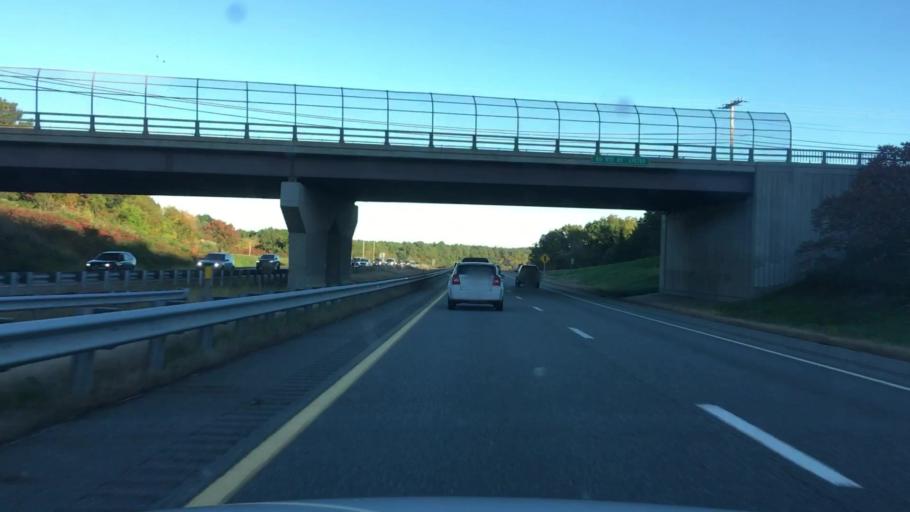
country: US
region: New Hampshire
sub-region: Rockingham County
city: Exeter
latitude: 43.0014
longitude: -70.9475
